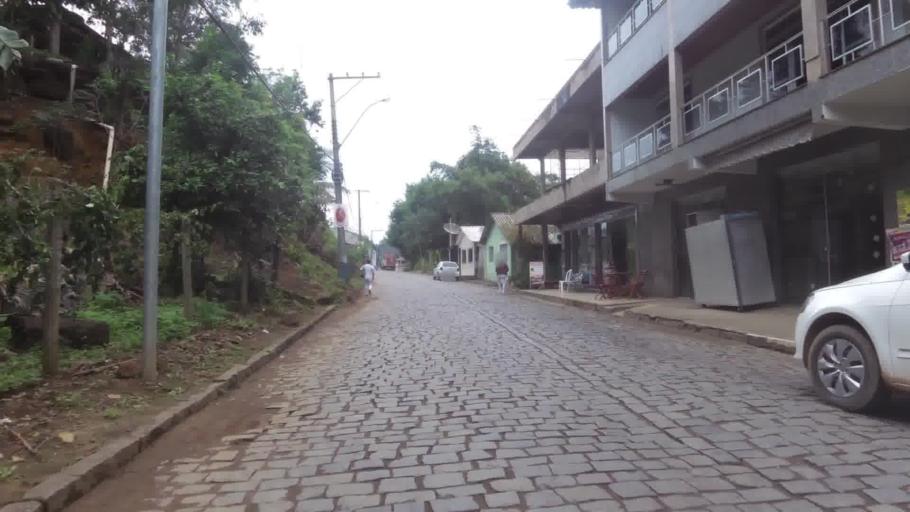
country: BR
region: Espirito Santo
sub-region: Iconha
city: Iconha
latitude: -20.7673
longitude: -40.8334
